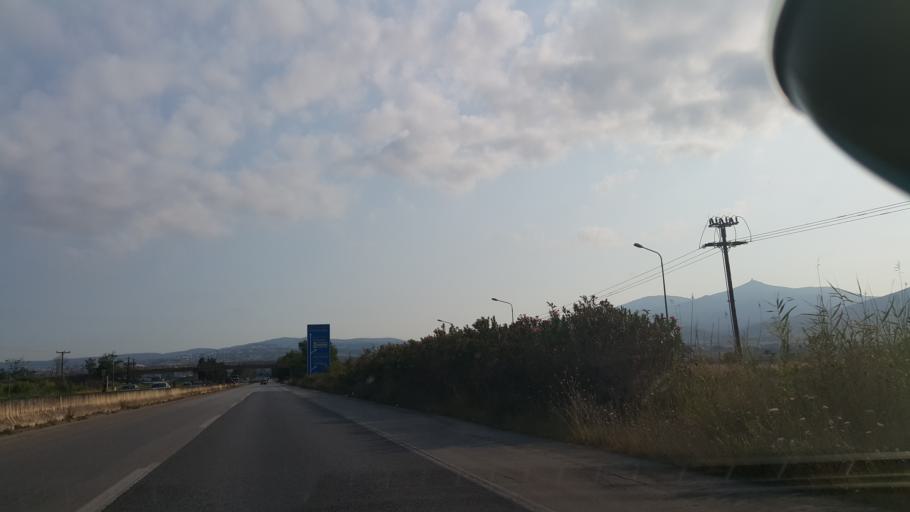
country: GR
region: Central Macedonia
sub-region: Nomos Thessalonikis
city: Neo Rysi
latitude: 40.5126
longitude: 23.0087
